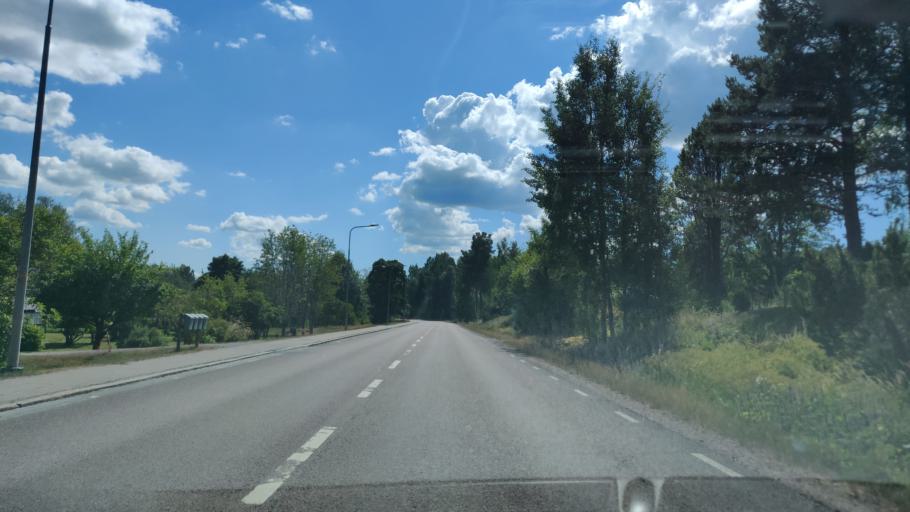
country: SE
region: Vaermland
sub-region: Hagfors Kommun
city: Ekshaerad
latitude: 60.1836
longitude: 13.4963
